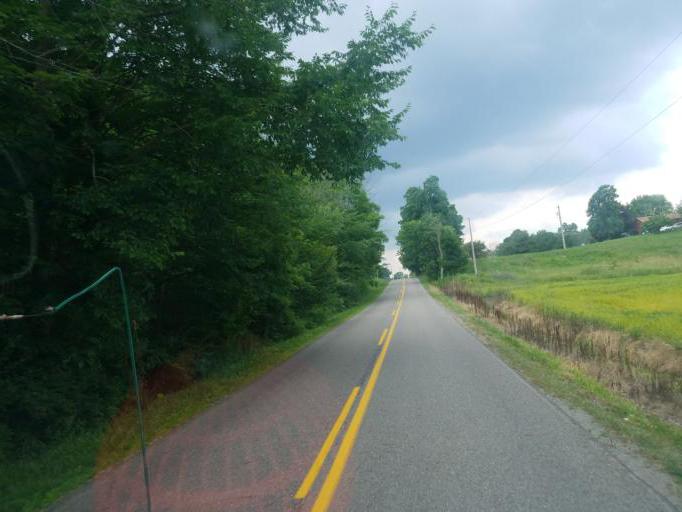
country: US
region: Ohio
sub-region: Mahoning County
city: Sebring
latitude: 40.9741
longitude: -80.9508
